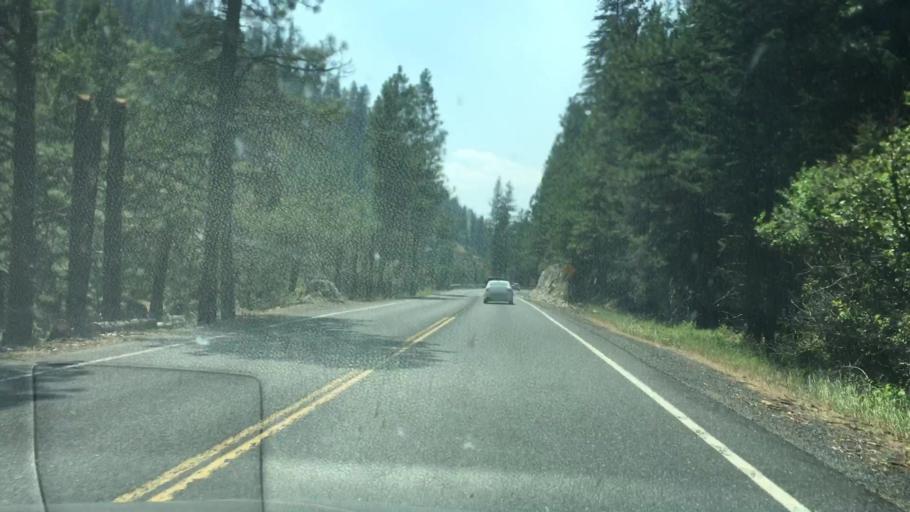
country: US
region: Idaho
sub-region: Valley County
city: McCall
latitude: 45.1276
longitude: -116.2895
